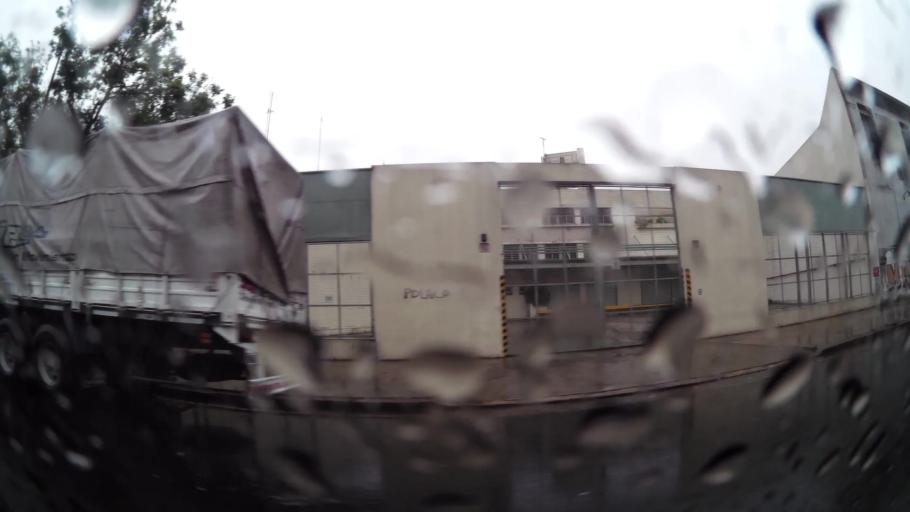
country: AR
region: Buenos Aires
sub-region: Partido de Avellaneda
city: Avellaneda
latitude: -34.6436
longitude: -58.3986
